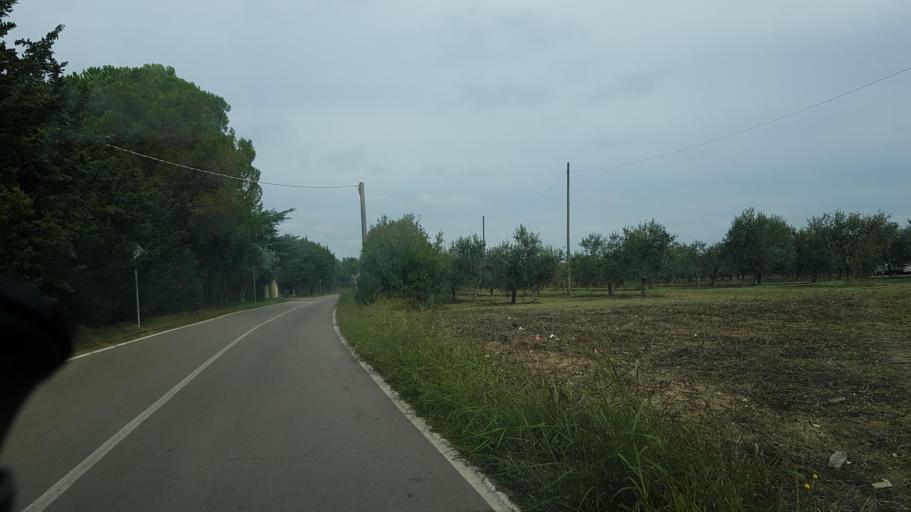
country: IT
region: Apulia
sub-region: Provincia di Lecce
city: Guagnano
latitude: 40.4065
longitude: 17.9500
